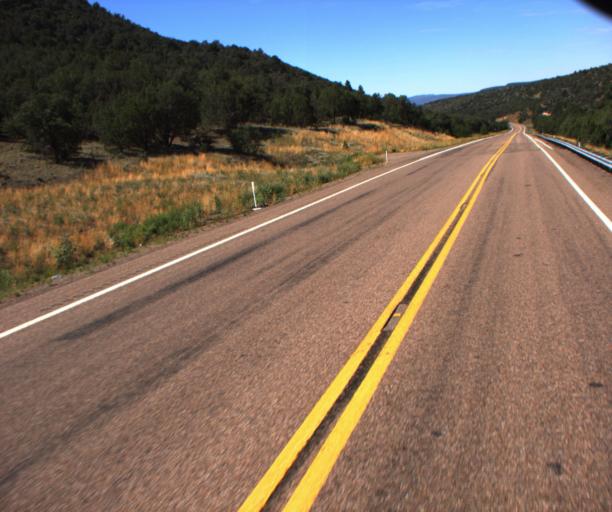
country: US
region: Arizona
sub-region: Navajo County
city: Cibecue
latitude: 33.8906
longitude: -110.3813
